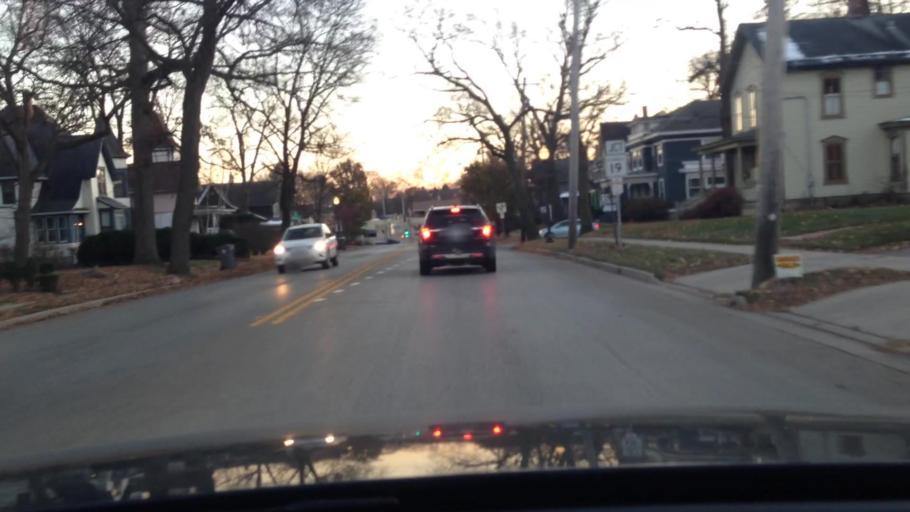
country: US
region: Illinois
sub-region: Kane County
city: Elgin
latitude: 42.0390
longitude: -88.2676
